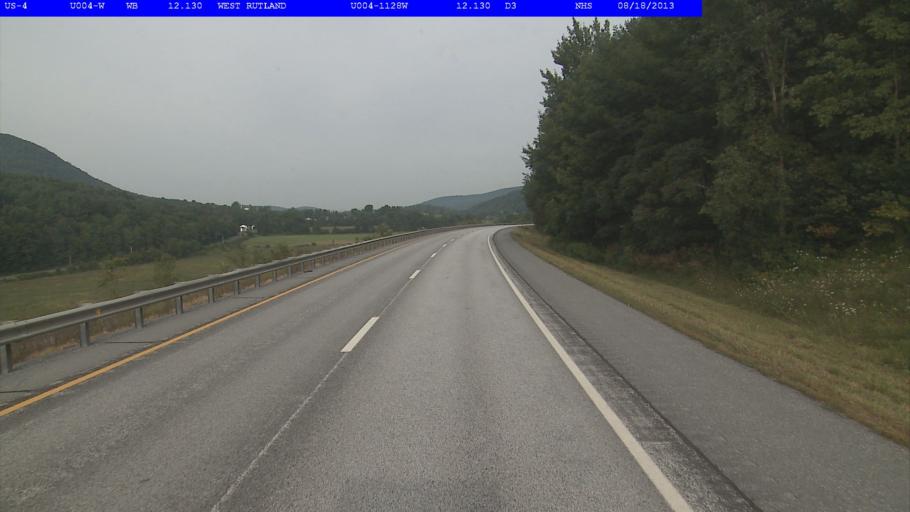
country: US
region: Vermont
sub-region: Rutland County
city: West Rutland
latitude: 43.6079
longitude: -73.0820
